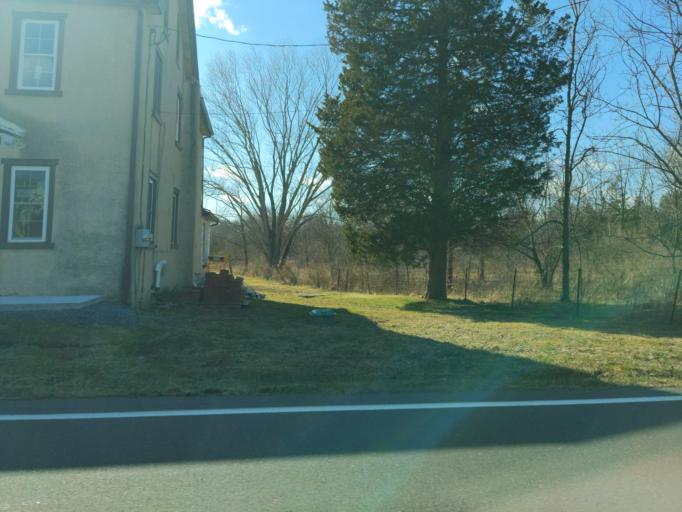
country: US
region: Pennsylvania
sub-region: Montgomery County
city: Red Hill
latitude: 40.3708
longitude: -75.4595
